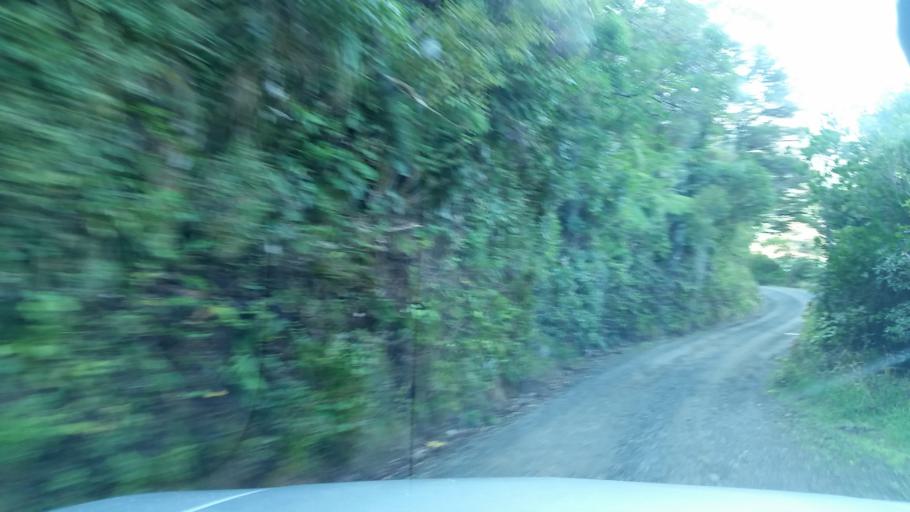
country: NZ
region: Marlborough
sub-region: Marlborough District
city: Picton
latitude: -41.1044
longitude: 173.6558
